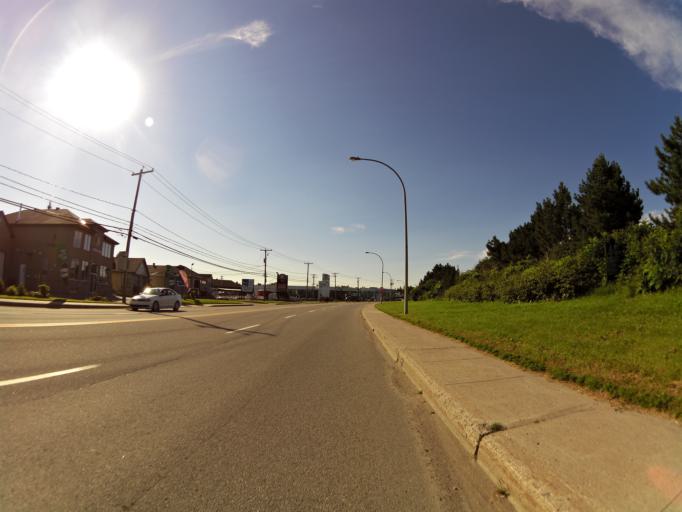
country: CA
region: Quebec
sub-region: Outaouais
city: Gatineau
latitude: 45.4743
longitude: -75.7414
